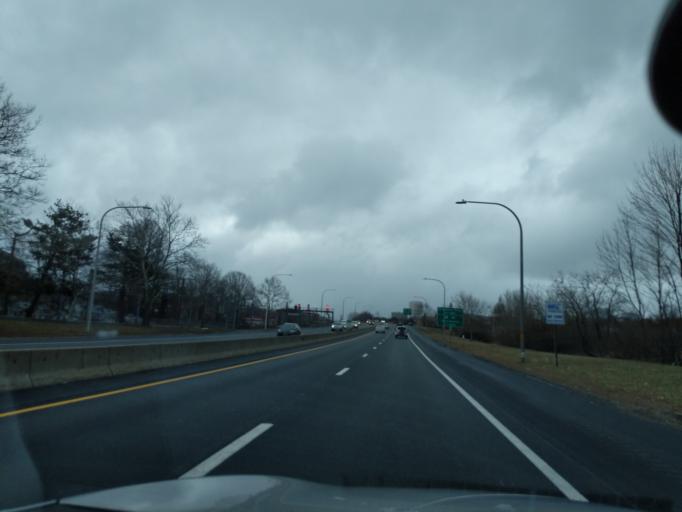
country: US
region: Rhode Island
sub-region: Providence County
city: Providence
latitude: 41.8402
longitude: -71.4177
